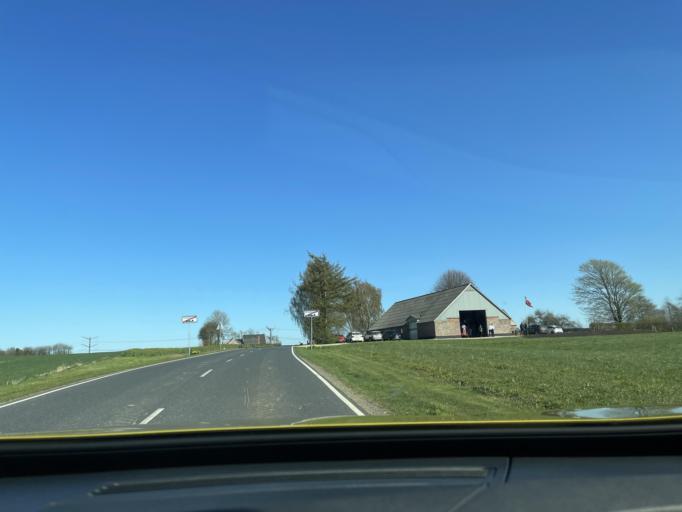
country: DK
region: Central Jutland
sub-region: Silkeborg Kommune
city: Kjellerup
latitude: 56.2526
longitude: 9.4365
